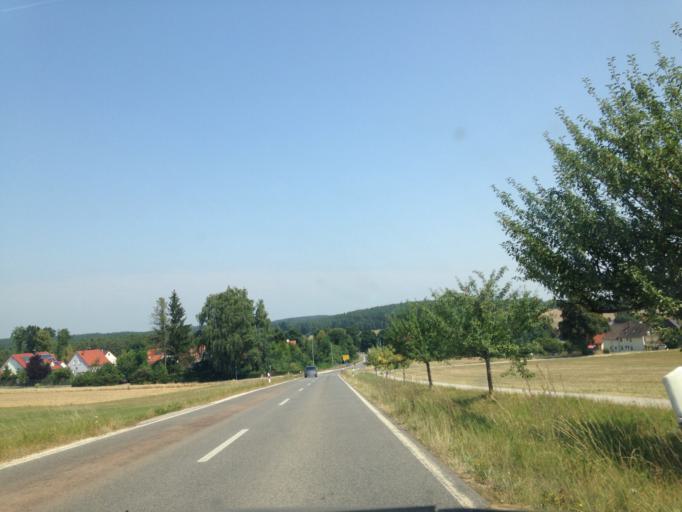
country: DE
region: Bavaria
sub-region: Regierungsbezirk Mittelfranken
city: Hilpoltstein
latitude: 49.1453
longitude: 11.2149
